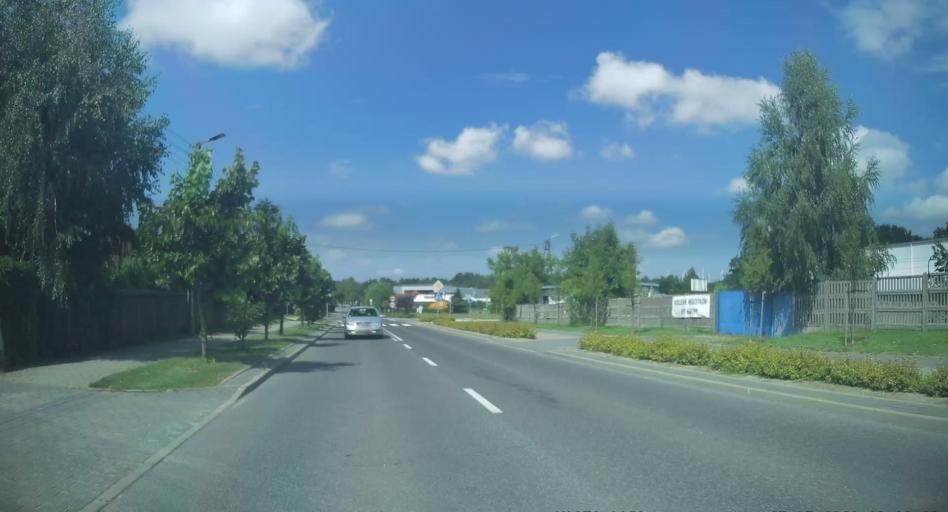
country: PL
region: Lodz Voivodeship
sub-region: Powiat rawski
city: Rawa Mazowiecka
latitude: 51.7526
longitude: 20.2387
